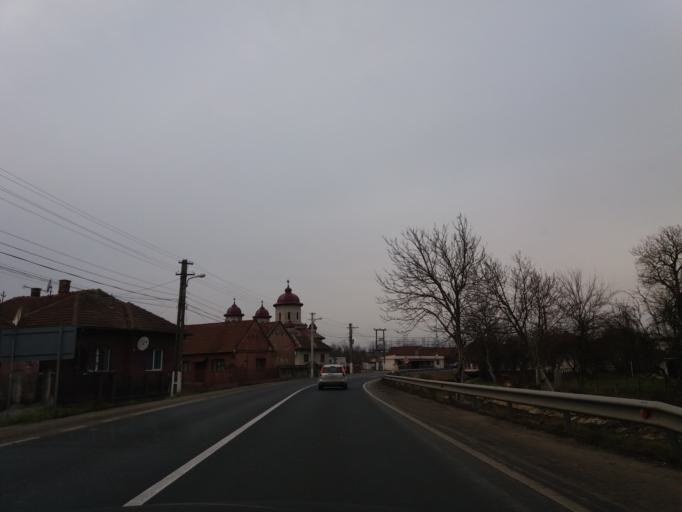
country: RO
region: Hunedoara
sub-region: Comuna Bacia
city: Bacia
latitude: 45.7768
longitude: 23.0011
